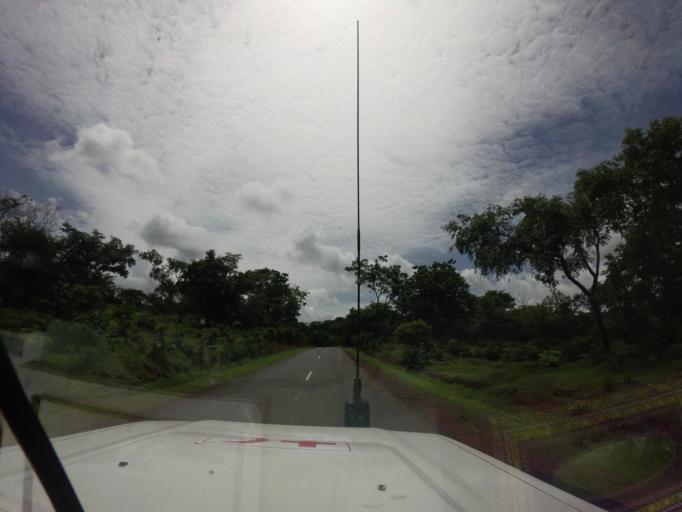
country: SL
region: Northern Province
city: Gberia Fotombu
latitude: 10.1723
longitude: -11.1993
